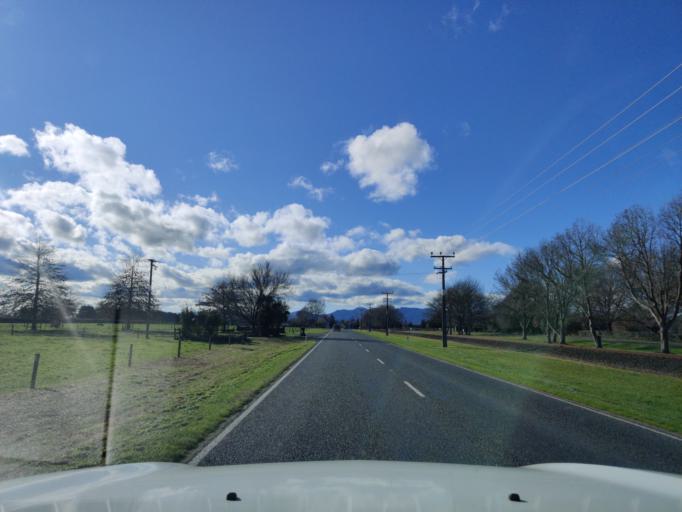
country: NZ
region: Waikato
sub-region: Matamata-Piako District
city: Matamata
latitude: -37.8324
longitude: 175.7670
